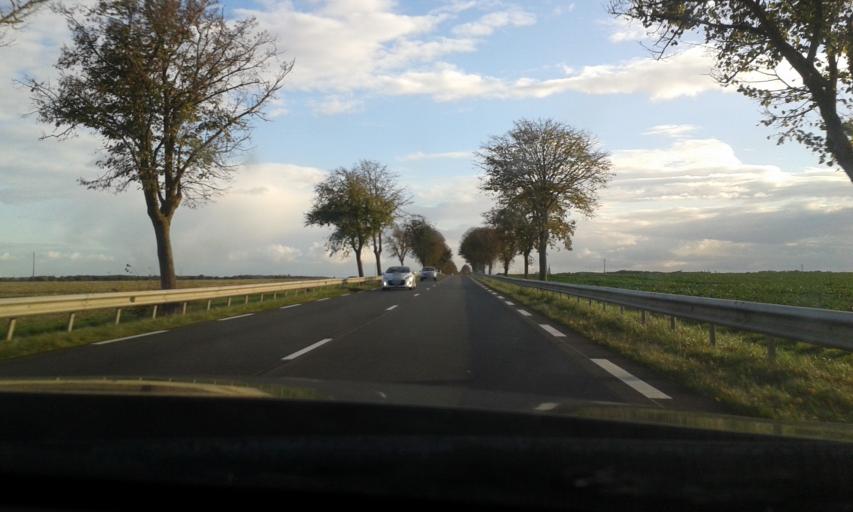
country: FR
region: Centre
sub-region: Departement d'Eure-et-Loir
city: Leves
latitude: 48.4967
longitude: 1.4690
